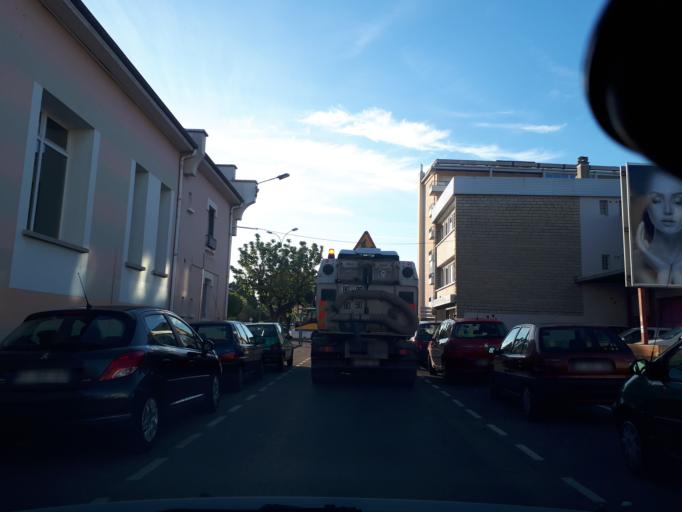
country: FR
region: Rhone-Alpes
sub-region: Departement de l'Isere
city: Bourgoin
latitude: 45.5901
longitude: 5.2810
